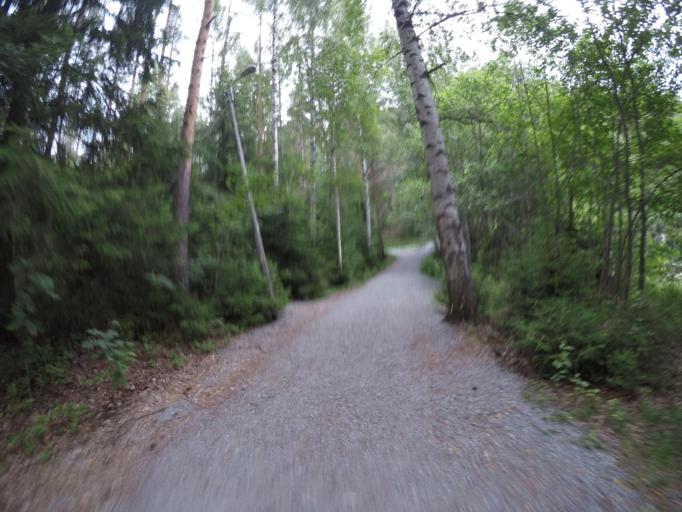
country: FI
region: Haeme
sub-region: Haemeenlinna
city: Haemeenlinna
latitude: 60.9980
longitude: 24.4122
